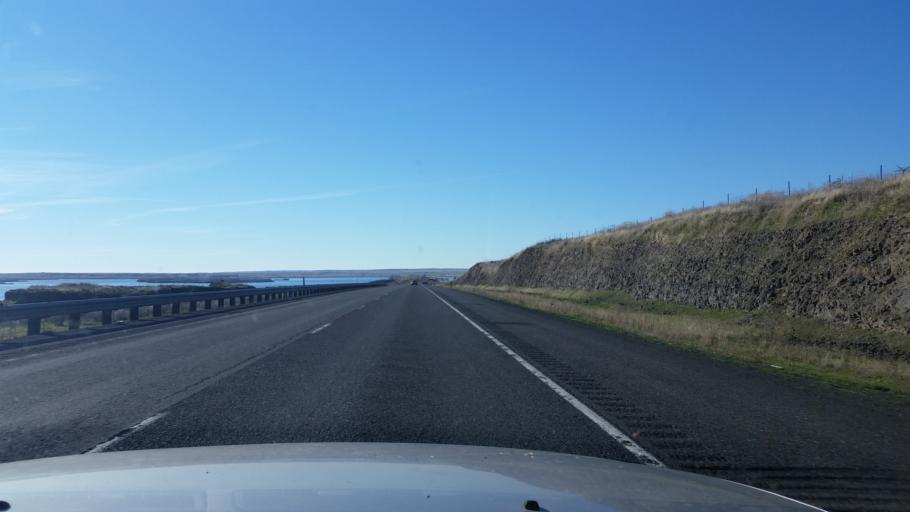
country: US
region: Washington
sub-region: Adams County
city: Ritzville
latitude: 47.2651
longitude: -118.0708
